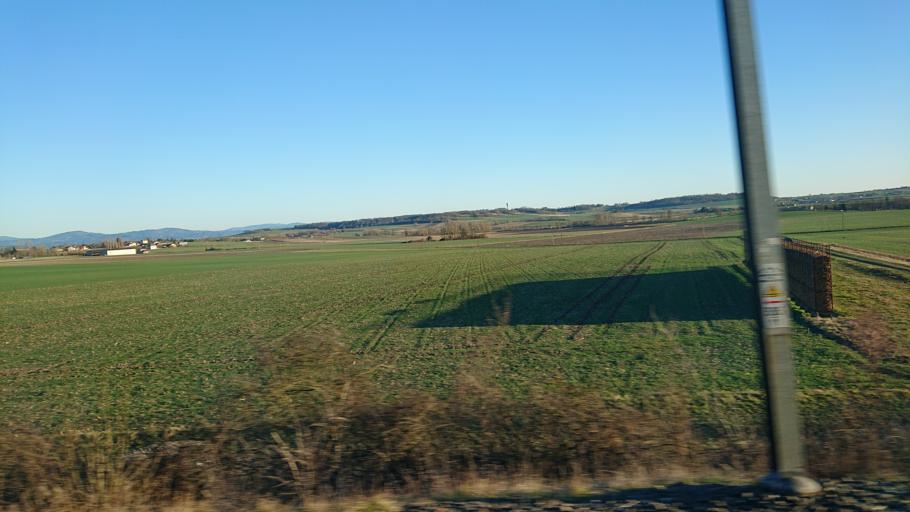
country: FR
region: Auvergne
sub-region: Departement du Puy-de-Dome
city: Randan
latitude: 46.0033
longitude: 3.3328
